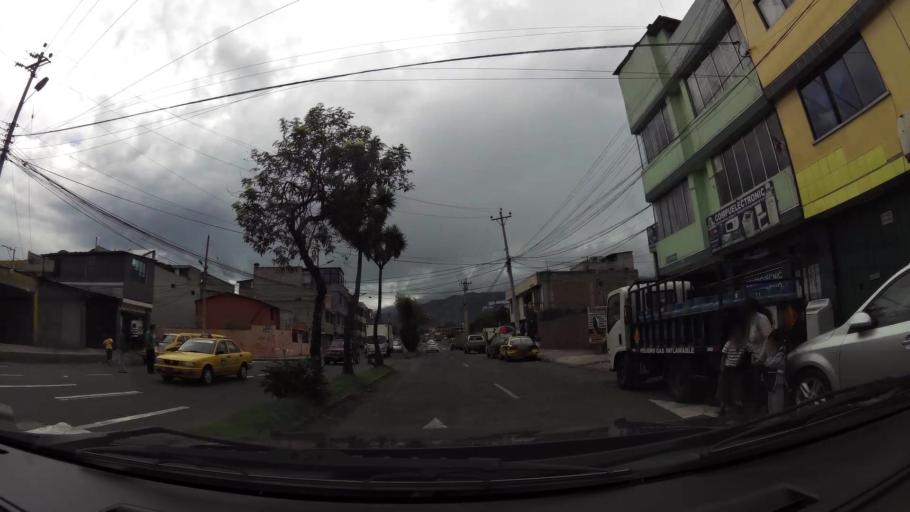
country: EC
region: Pichincha
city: Quito
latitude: -0.2749
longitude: -78.5448
